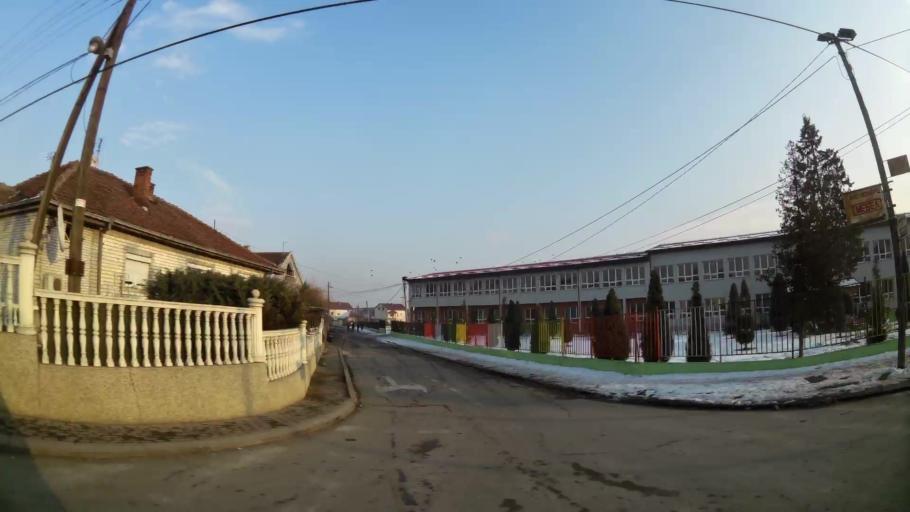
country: MK
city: Creshevo
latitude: 42.0132
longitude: 21.5102
